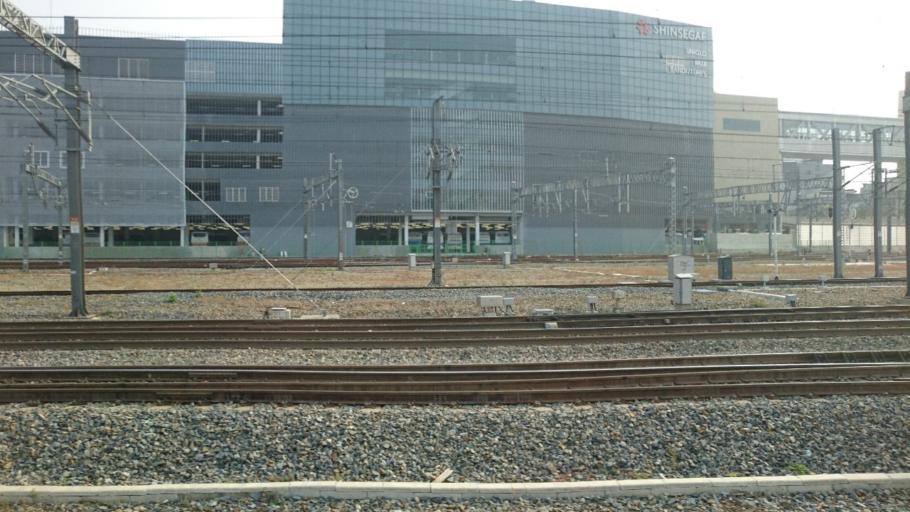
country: KR
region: Daegu
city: Daegu
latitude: 35.8806
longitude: 128.6323
